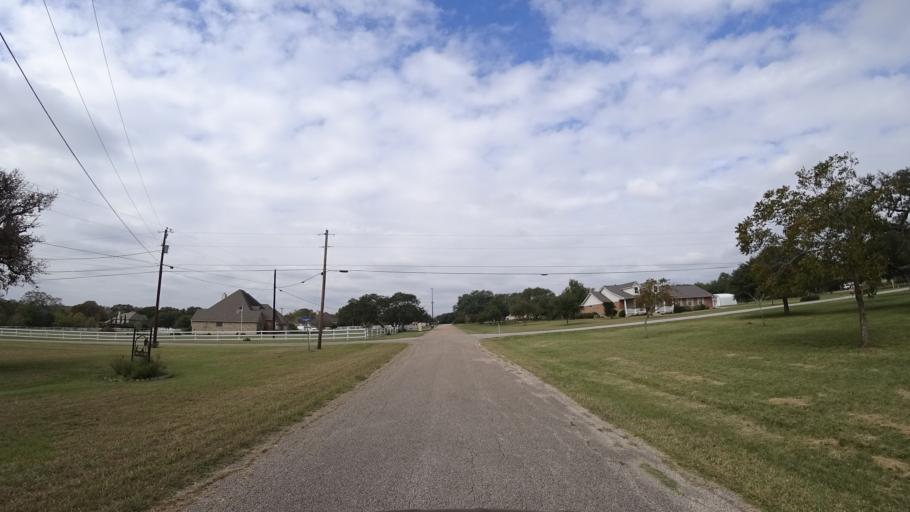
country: US
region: Texas
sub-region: Travis County
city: Shady Hollow
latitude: 30.2096
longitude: -97.8971
